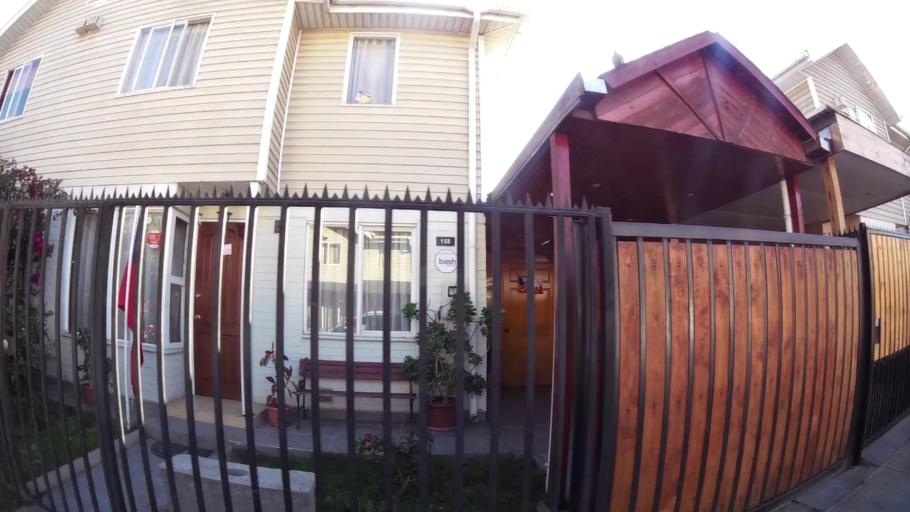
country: CL
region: Santiago Metropolitan
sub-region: Provincia de Santiago
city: Lo Prado
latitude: -33.4932
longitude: -70.7770
